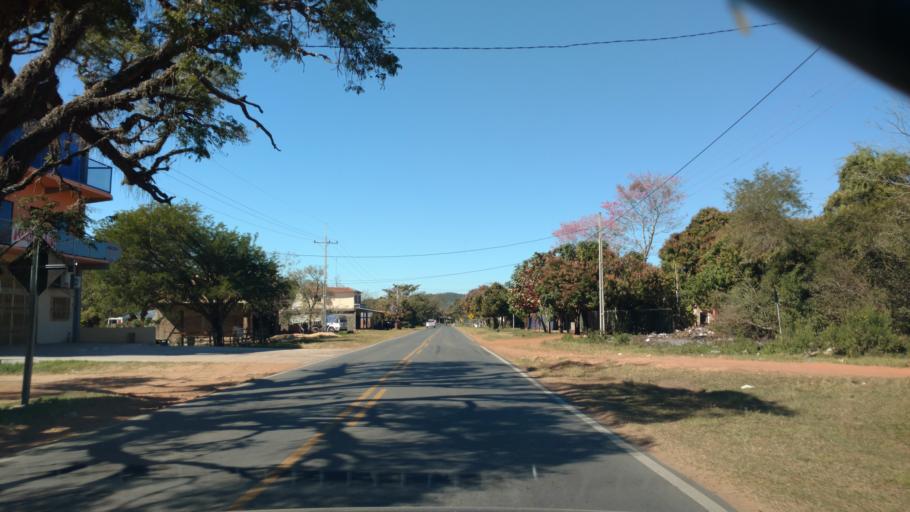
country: PY
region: Paraguari
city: Pirayu
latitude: -25.4552
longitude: -57.2724
